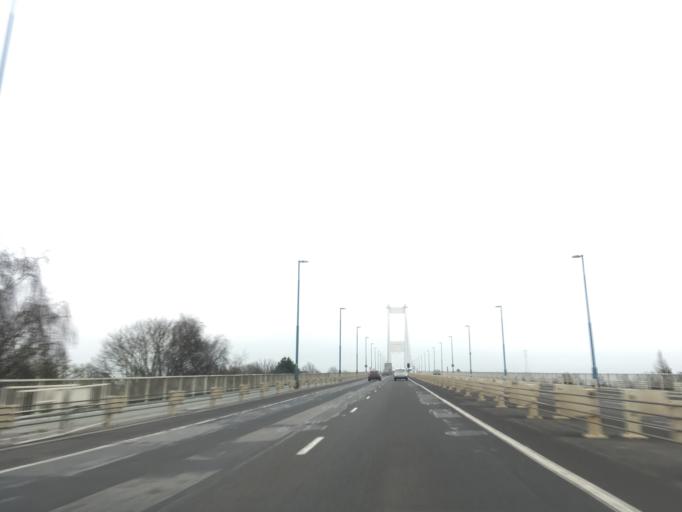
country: GB
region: Wales
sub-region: Monmouthshire
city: Chepstow
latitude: 51.6160
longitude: -2.6559
